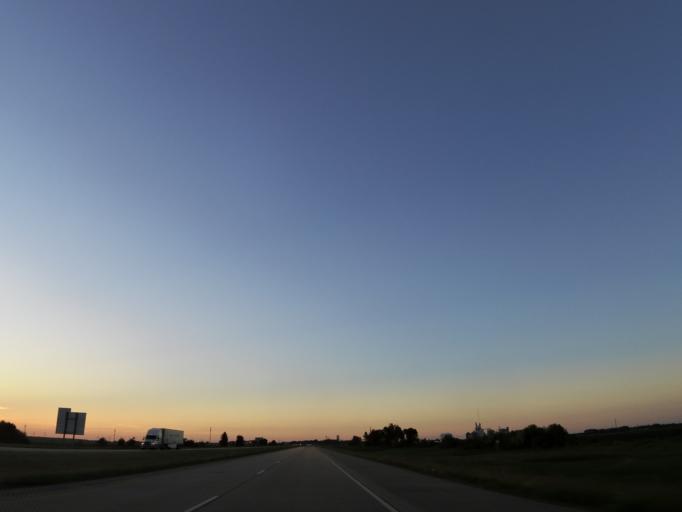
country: US
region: North Dakota
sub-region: Grand Forks County
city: Grand Forks
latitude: 47.9512
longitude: -97.0933
